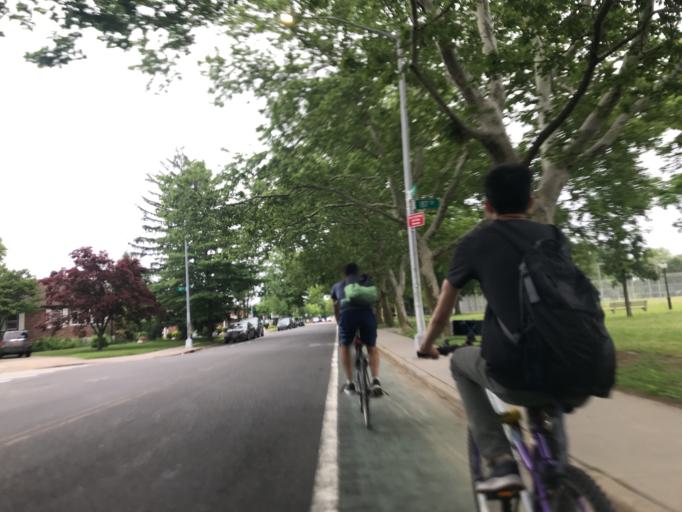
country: US
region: New York
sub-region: Queens County
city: Jamaica
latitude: 40.7463
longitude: -73.7910
